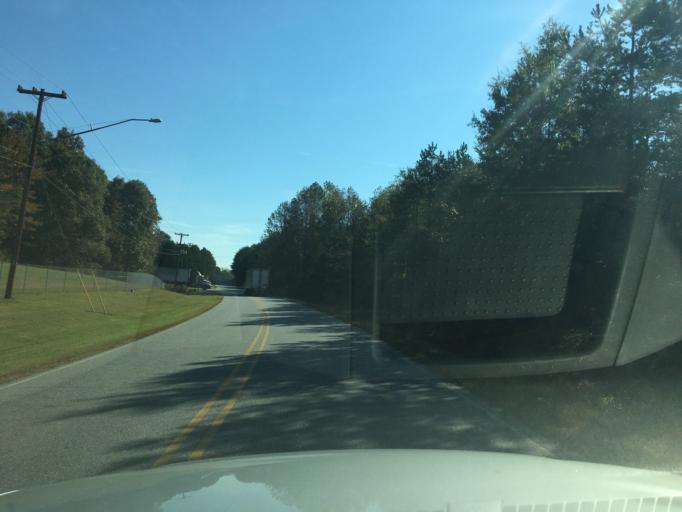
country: US
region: North Carolina
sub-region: Catawba County
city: Conover
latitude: 35.7155
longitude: -81.2605
